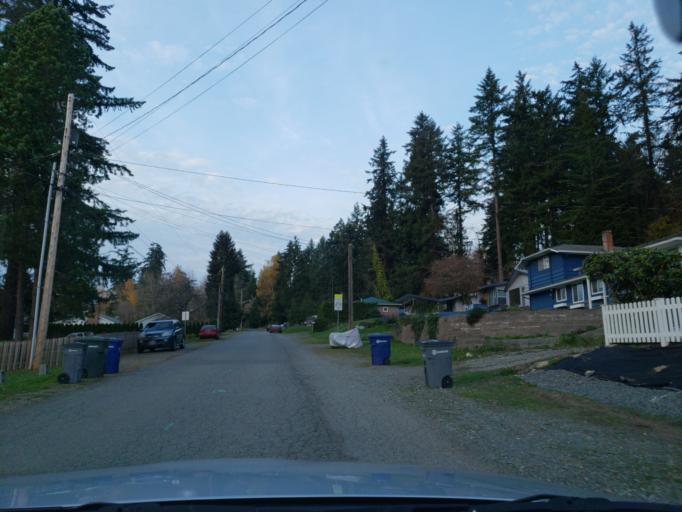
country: US
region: Washington
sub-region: King County
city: Bothell
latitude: 47.7661
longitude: -122.2033
